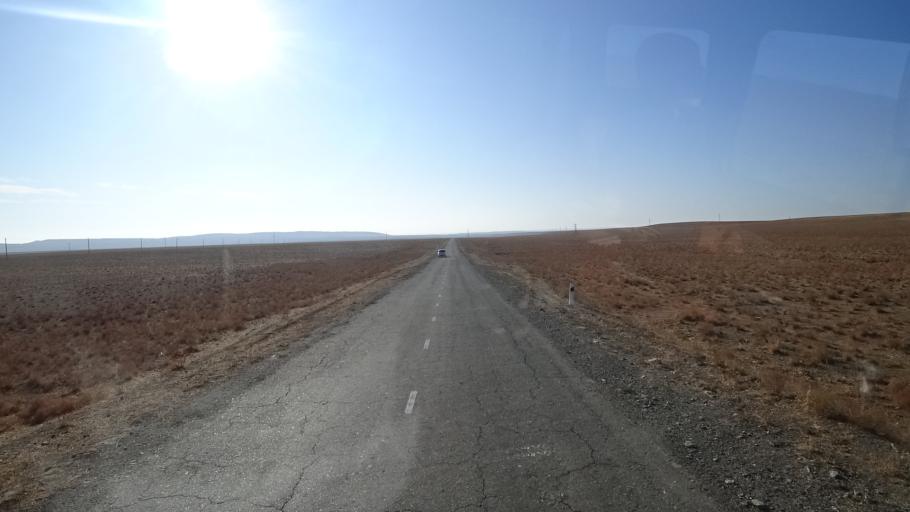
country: UZ
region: Navoiy
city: Karmana Shahri
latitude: 40.2706
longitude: 65.5281
